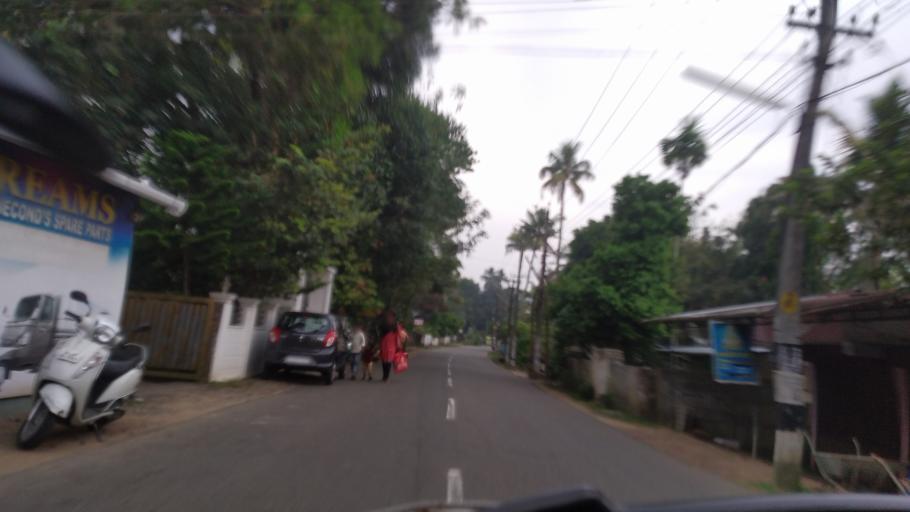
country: IN
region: Kerala
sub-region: Ernakulam
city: Elur
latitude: 10.1363
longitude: 76.2473
